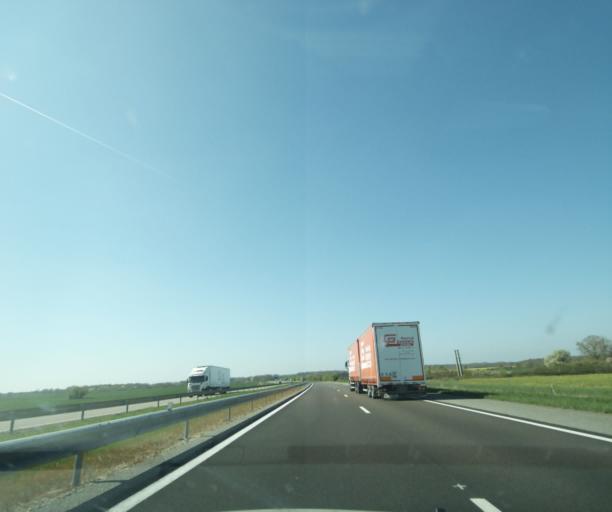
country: FR
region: Centre
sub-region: Departement du Loiret
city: Briare
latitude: 47.6322
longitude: 2.7840
